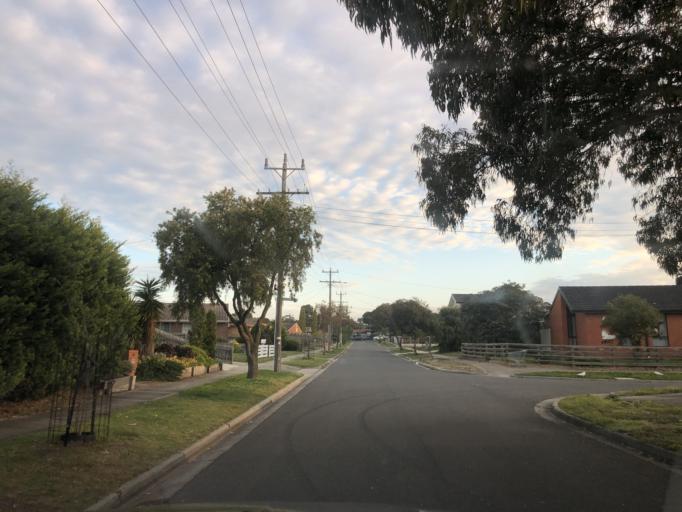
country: AU
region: Victoria
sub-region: Casey
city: Hallam
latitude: -38.0300
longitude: 145.2642
